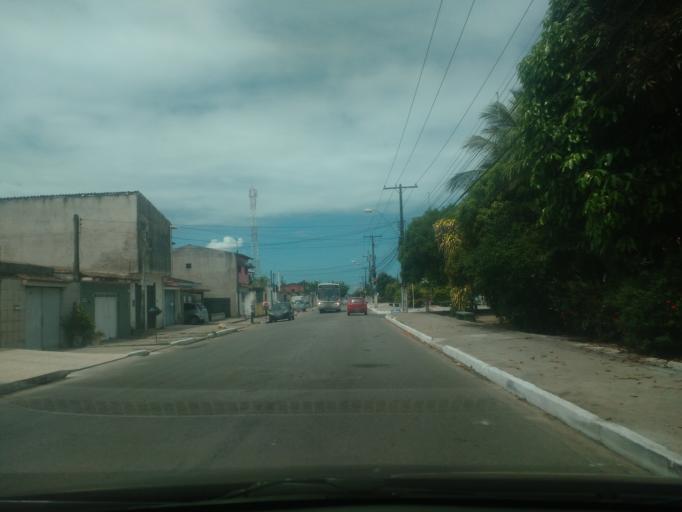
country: BR
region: Alagoas
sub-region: Satuba
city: Satuba
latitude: -9.5538
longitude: -35.7651
